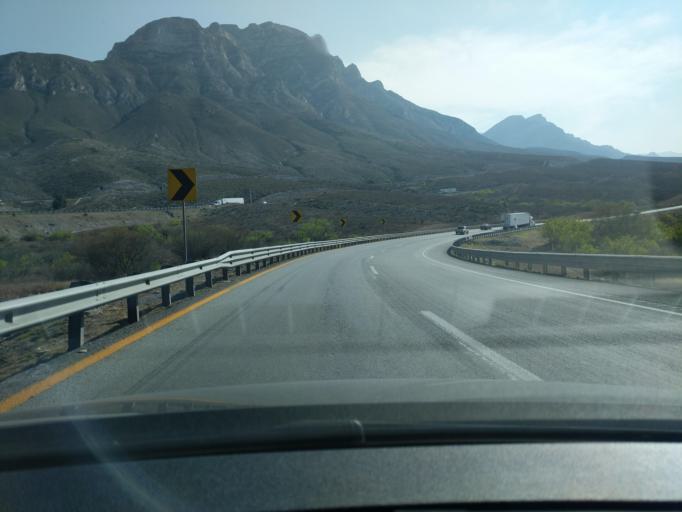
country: MX
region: Nuevo Leon
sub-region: Garcia
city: Las Torres de Guadalupe
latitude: 25.6559
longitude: -100.7202
